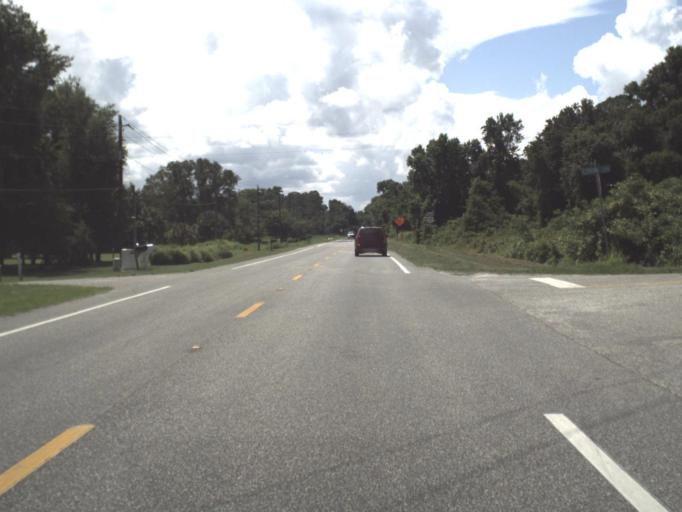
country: US
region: Florida
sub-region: Putnam County
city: Crescent City
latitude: 29.4557
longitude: -81.5175
